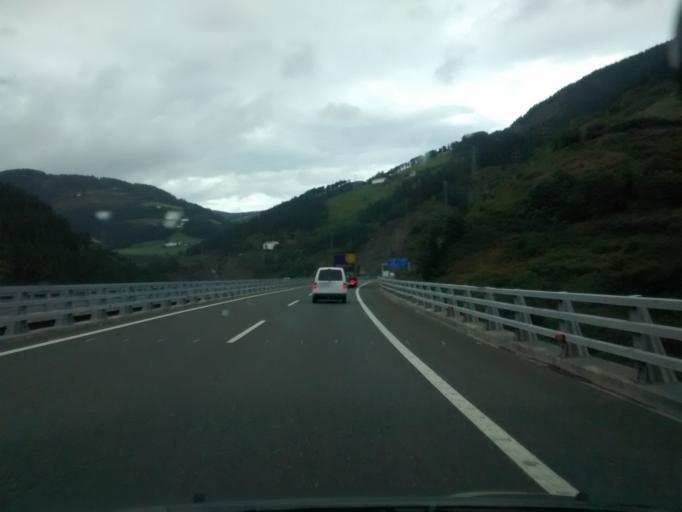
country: ES
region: Basque Country
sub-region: Provincia de Guipuzcoa
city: Elgoibar
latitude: 43.1833
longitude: -2.4283
